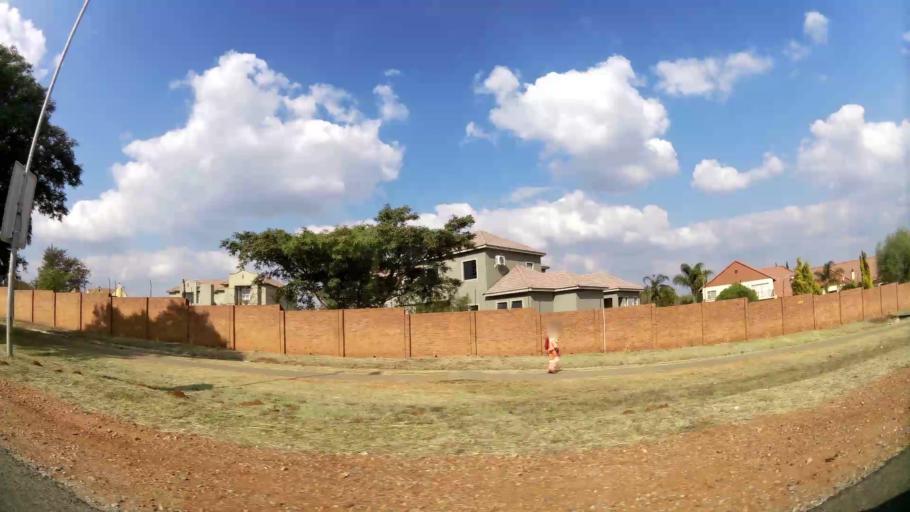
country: ZA
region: Gauteng
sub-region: City of Tshwane Metropolitan Municipality
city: Centurion
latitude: -25.8751
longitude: 28.2309
